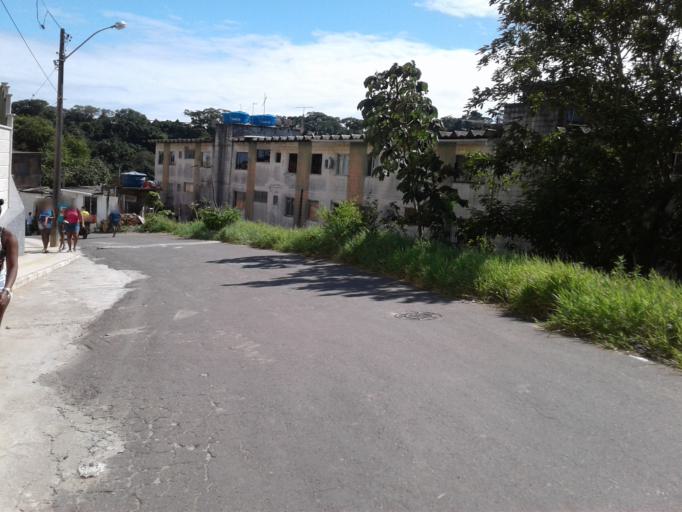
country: BR
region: Bahia
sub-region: Salvador
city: Salvador
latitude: -12.9118
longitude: -38.4664
